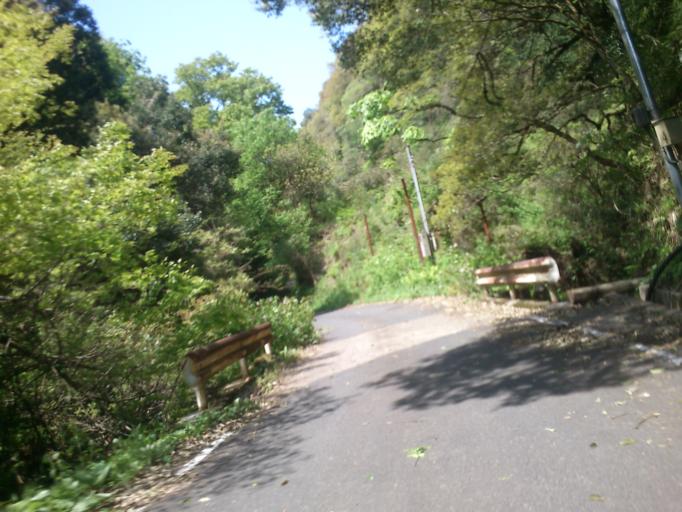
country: JP
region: Kyoto
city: Miyazu
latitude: 35.6717
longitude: 135.2370
